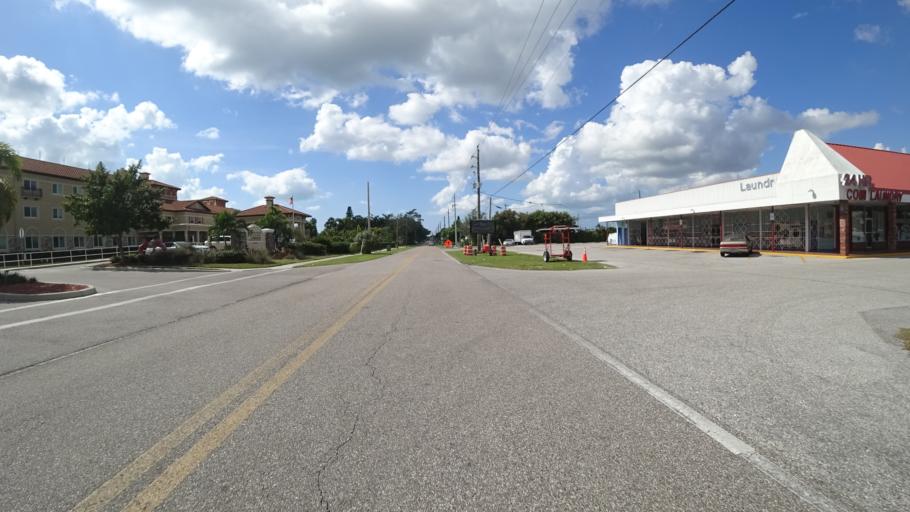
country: US
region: Florida
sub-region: Manatee County
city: Whitfield
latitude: 27.4184
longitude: -82.5766
